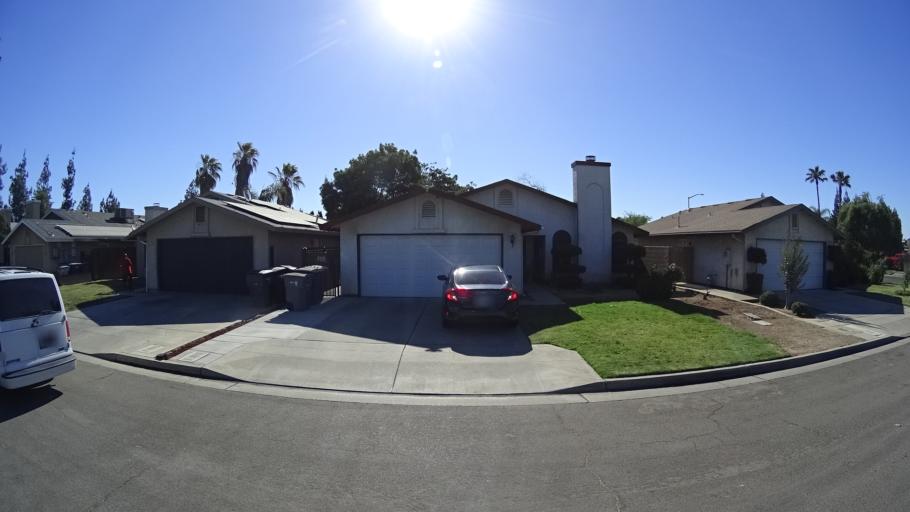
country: US
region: California
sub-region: Fresno County
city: West Park
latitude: 36.7782
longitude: -119.8590
